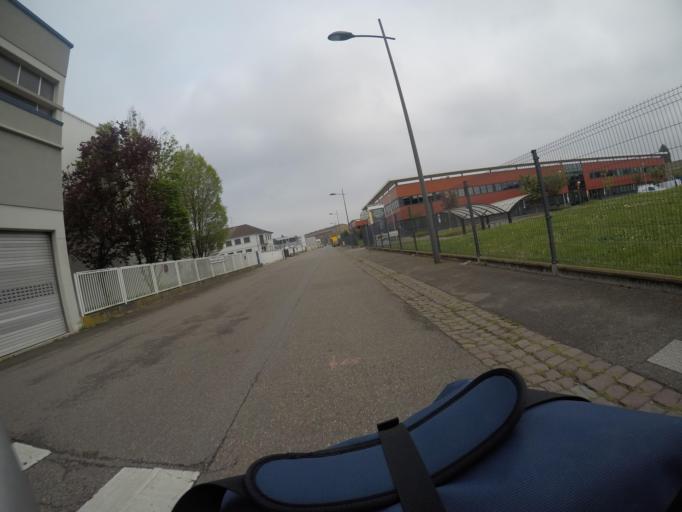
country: FR
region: Alsace
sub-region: Departement du Bas-Rhin
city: Strasbourg
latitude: 48.5577
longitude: 7.7430
